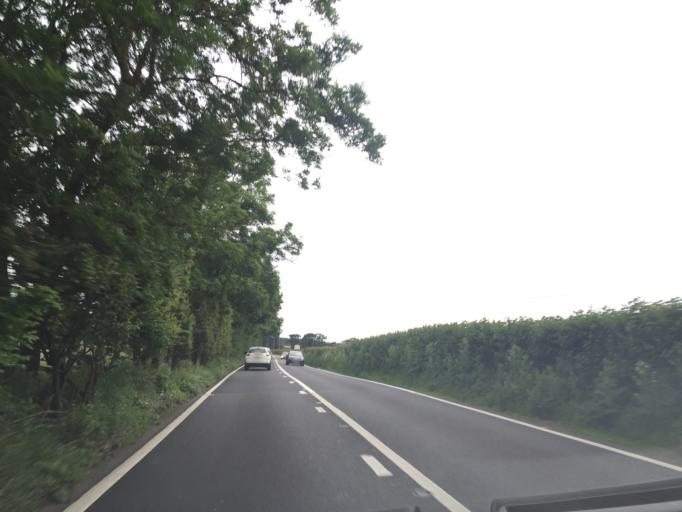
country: GB
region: England
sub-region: Dorset
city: Lytchett Matravers
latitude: 50.7868
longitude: -2.0606
